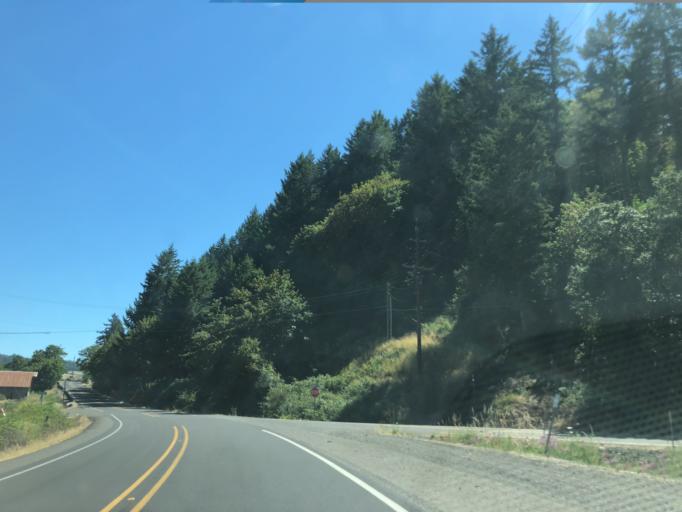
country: US
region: Oregon
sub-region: Douglas County
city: Yoncalla
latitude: 43.5807
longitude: -123.2810
